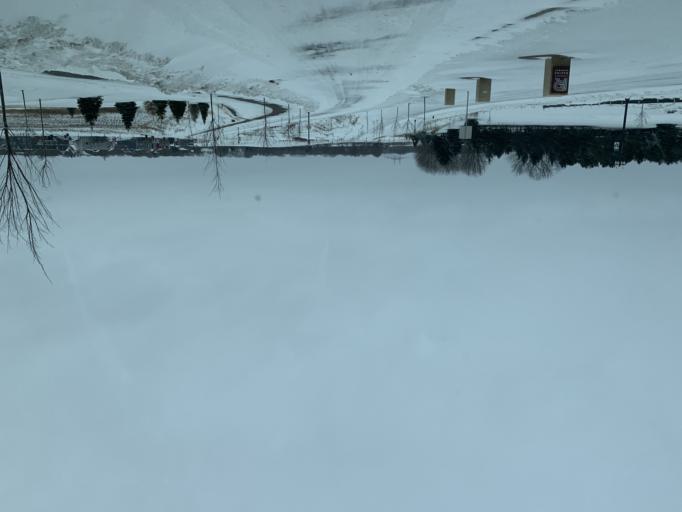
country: US
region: Minnesota
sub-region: Washington County
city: Cottage Grove
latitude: 44.8551
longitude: -92.9178
